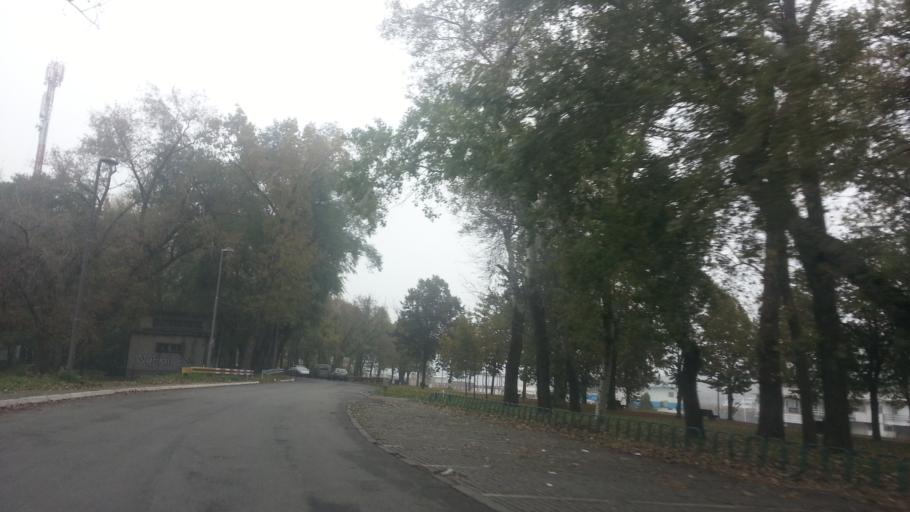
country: RS
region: Central Serbia
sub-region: Belgrade
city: Stari Grad
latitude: 44.8172
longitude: 20.4449
